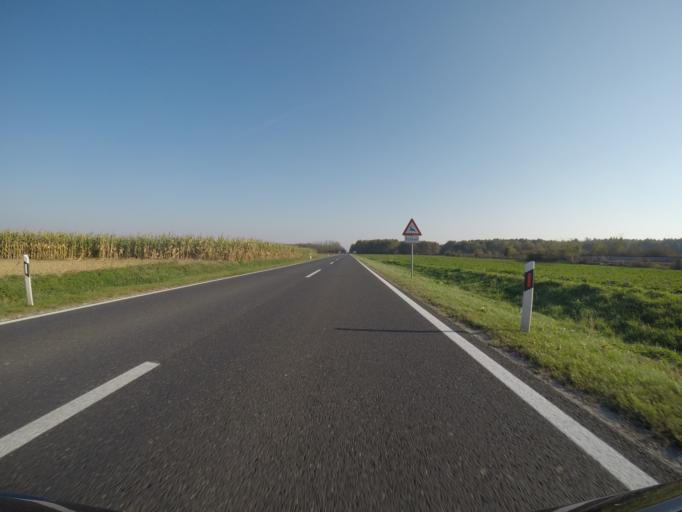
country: HR
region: Koprivnicko-Krizevacka
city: Kalinovac
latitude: 46.0016
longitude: 17.1141
